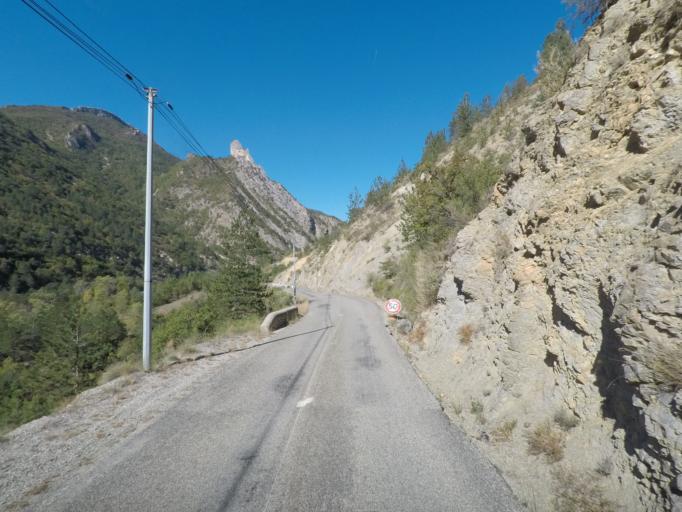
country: FR
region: Rhone-Alpes
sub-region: Departement de la Drome
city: Die
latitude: 44.6461
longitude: 5.2938
